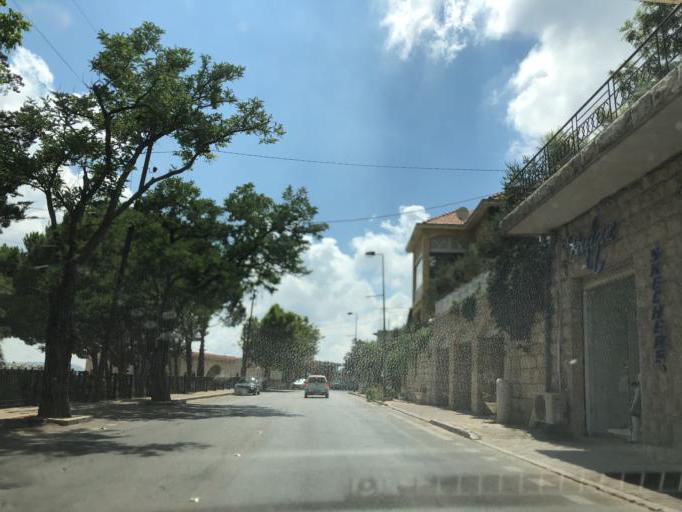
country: LB
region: Mont-Liban
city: Beit ed Dine
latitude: 33.6972
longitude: 35.5605
